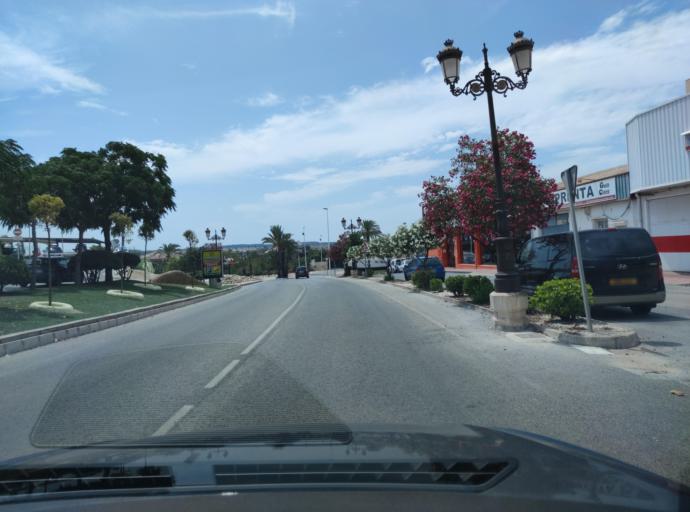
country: ES
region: Valencia
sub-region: Provincia de Alicante
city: Guardamar del Segura
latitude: 38.0956
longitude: -0.6601
